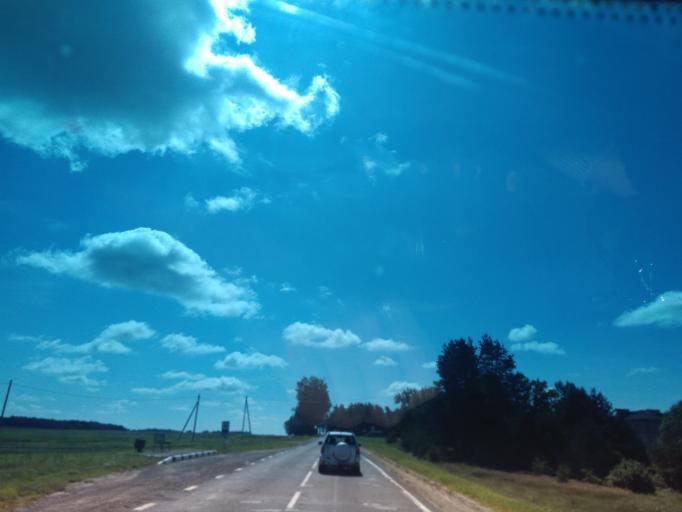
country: BY
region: Minsk
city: Uzda
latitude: 53.2915
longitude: 27.2395
